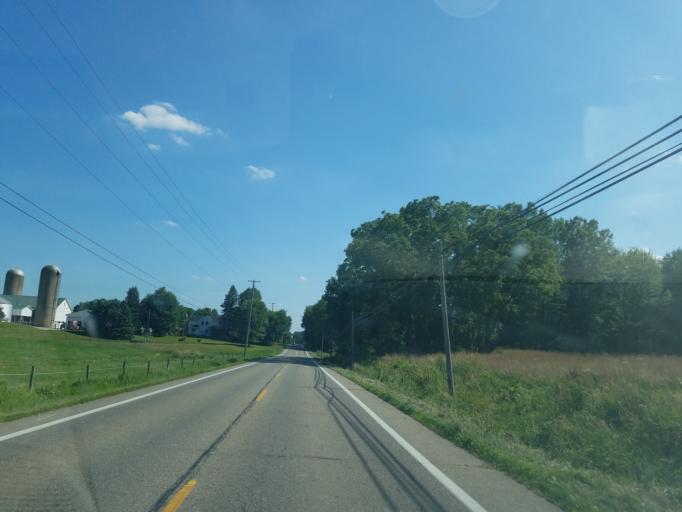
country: US
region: Ohio
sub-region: Portage County
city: Ravenna
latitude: 41.1947
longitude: -81.2463
